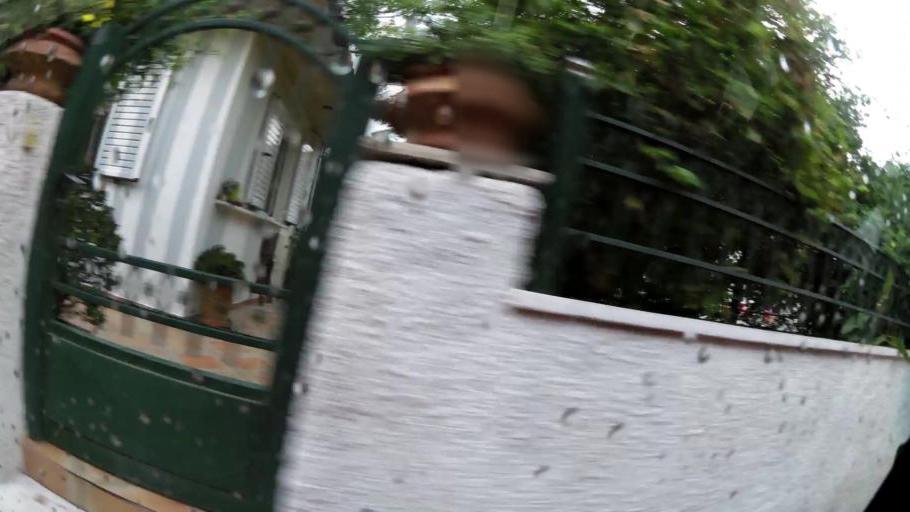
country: GR
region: Attica
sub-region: Nomarchia Athinas
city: Agioi Anargyroi
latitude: 38.0322
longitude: 23.7278
